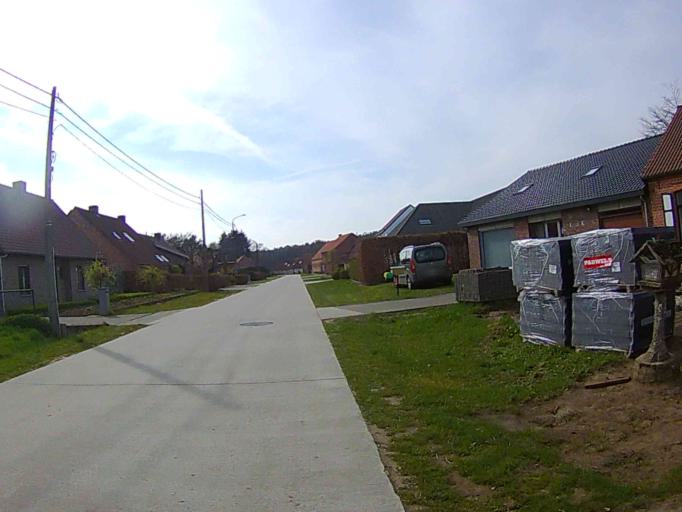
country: BE
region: Flanders
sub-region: Provincie Antwerpen
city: Kasterlee
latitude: 51.2242
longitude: 4.9489
